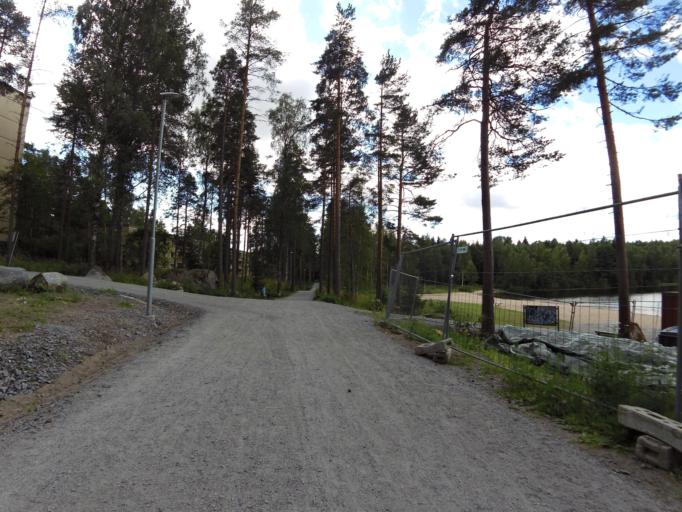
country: FI
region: Pirkanmaa
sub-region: Tampere
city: Pirkkala
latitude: 61.5074
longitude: 23.6156
